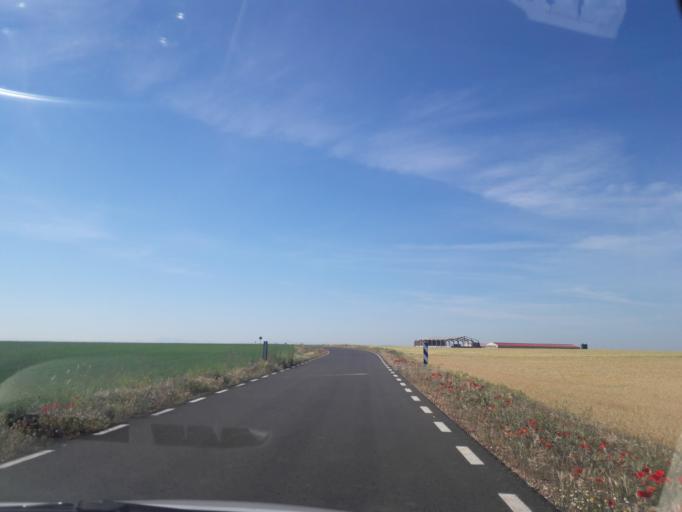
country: ES
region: Castille and Leon
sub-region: Provincia de Salamanca
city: Parada de Rubiales
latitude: 41.1308
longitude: -5.4302
